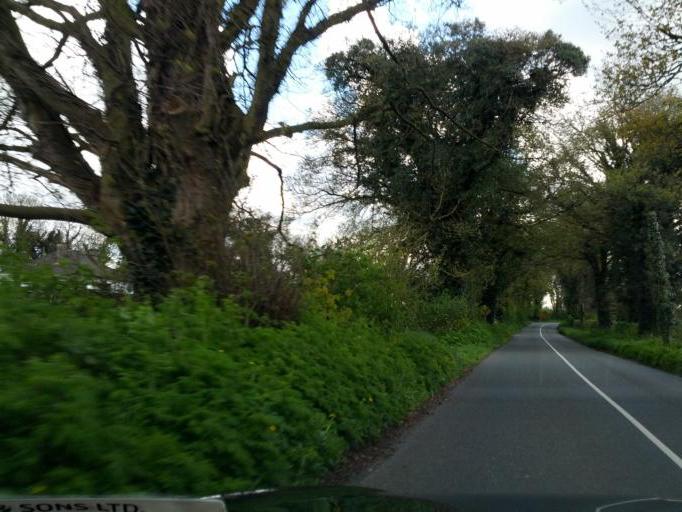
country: IE
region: Leinster
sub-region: An Mhi
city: Dunshaughlin
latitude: 53.5243
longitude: -6.6441
